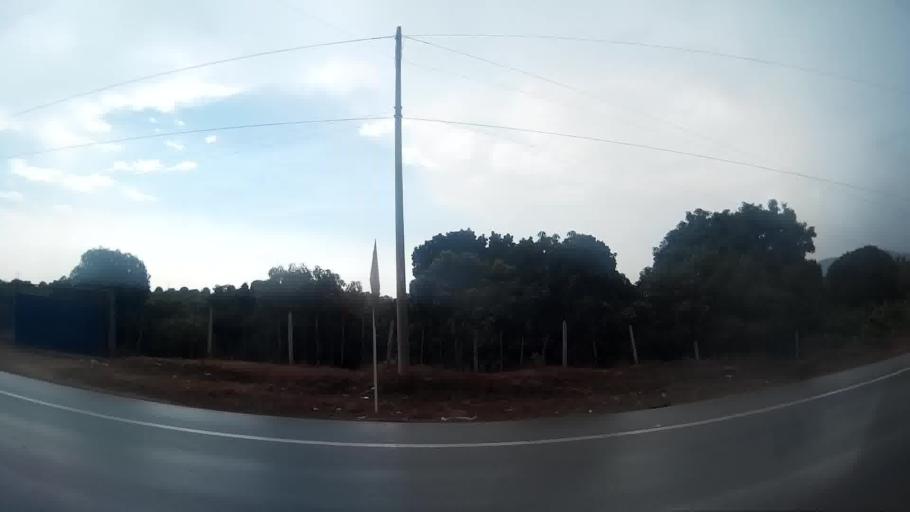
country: CO
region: Magdalena
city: Cienaga
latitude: 11.0197
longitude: -74.2111
